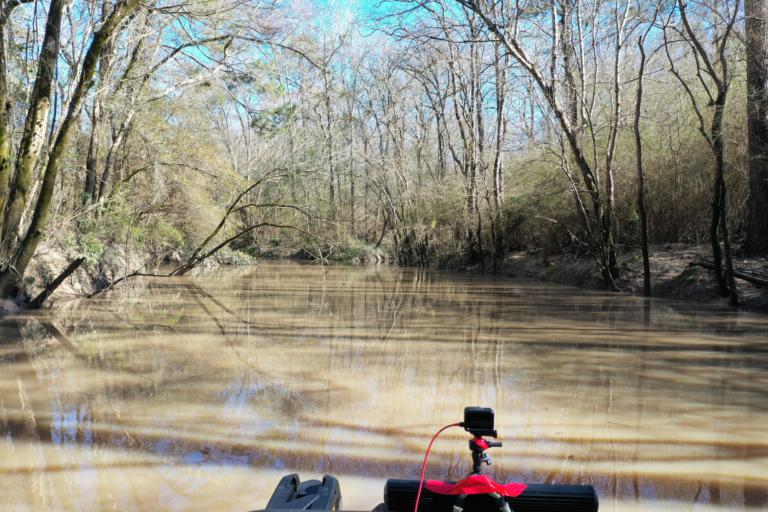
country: US
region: Louisiana
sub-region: Calcasieu Parish
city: Iowa
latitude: 30.3152
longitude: -93.0339
